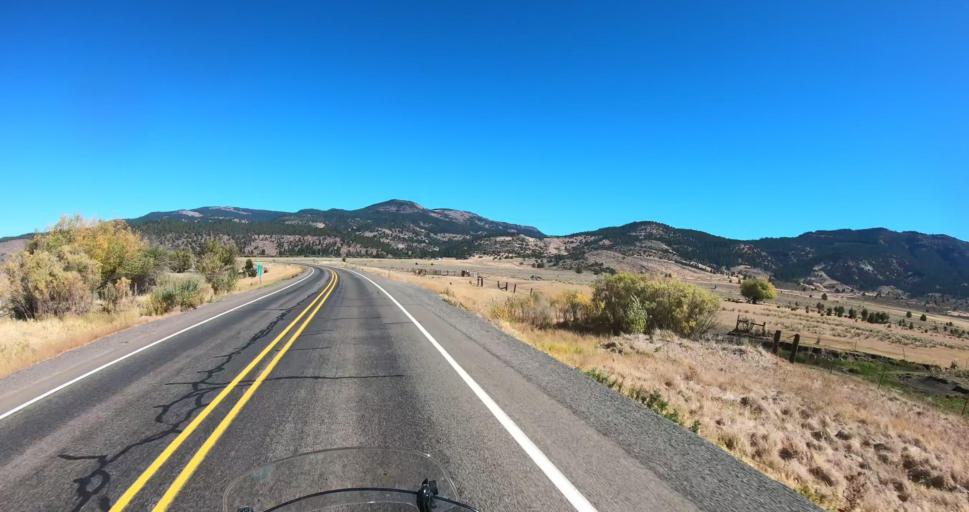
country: US
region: Oregon
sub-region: Lake County
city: Lakeview
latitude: 42.3277
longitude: -120.3035
